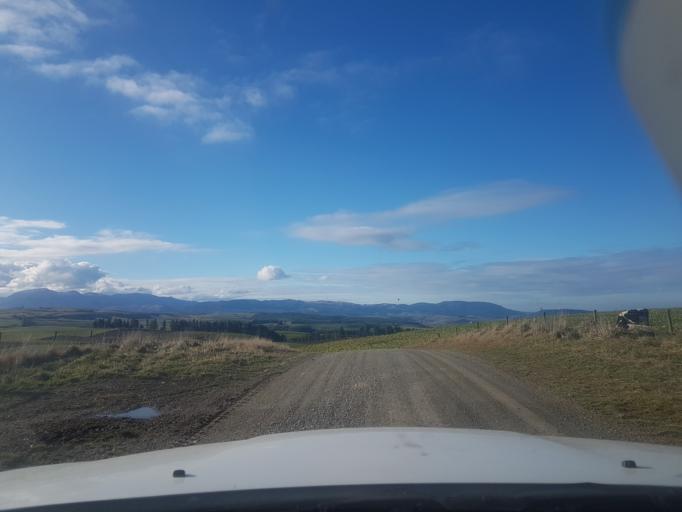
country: NZ
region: Canterbury
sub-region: Timaru District
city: Pleasant Point
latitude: -44.1686
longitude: 170.8902
